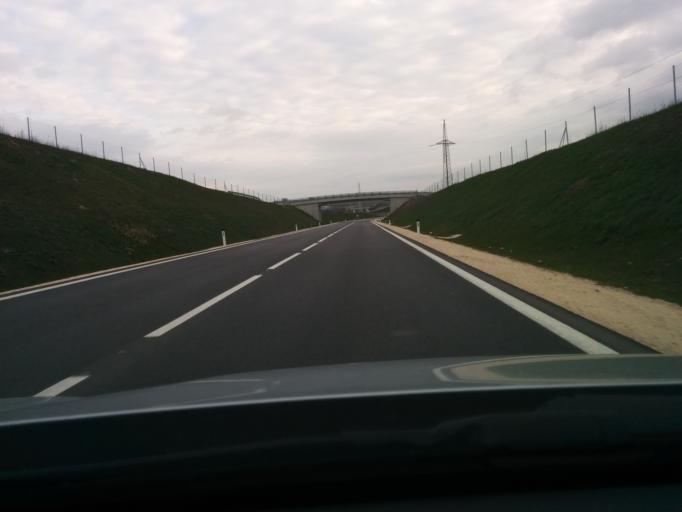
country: AT
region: Lower Austria
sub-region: Politischer Bezirk Mistelbach
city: Mistelbach
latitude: 48.5670
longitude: 16.5540
